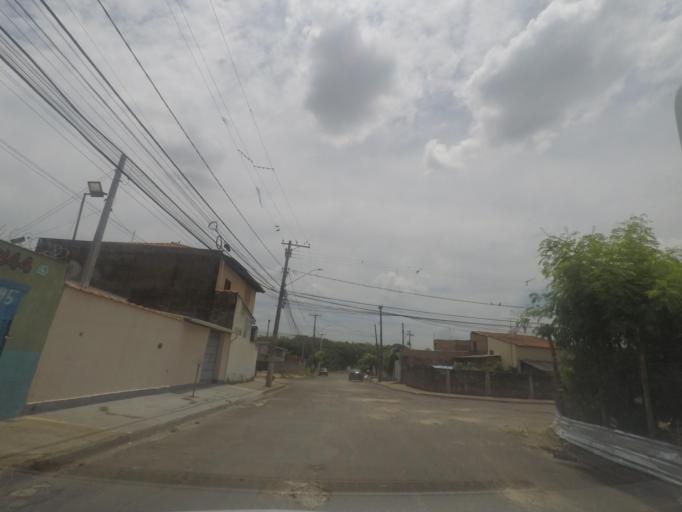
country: BR
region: Sao Paulo
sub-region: Nova Odessa
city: Nova Odessa
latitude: -22.7916
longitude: -47.2795
